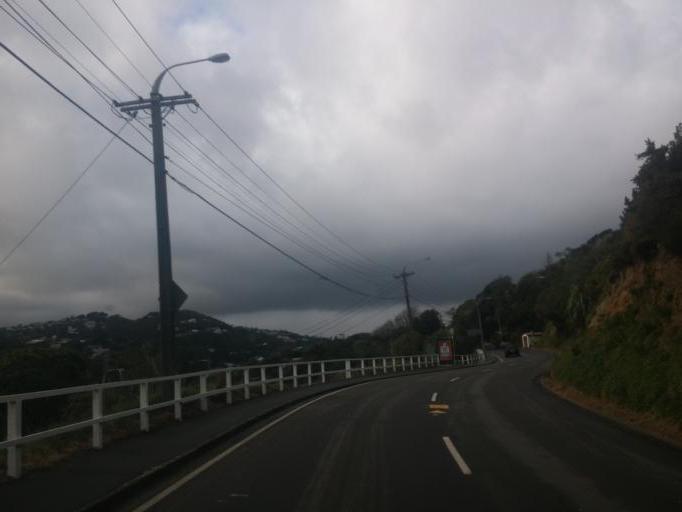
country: NZ
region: Wellington
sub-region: Wellington City
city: Kelburn
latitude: -41.2617
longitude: 174.7663
